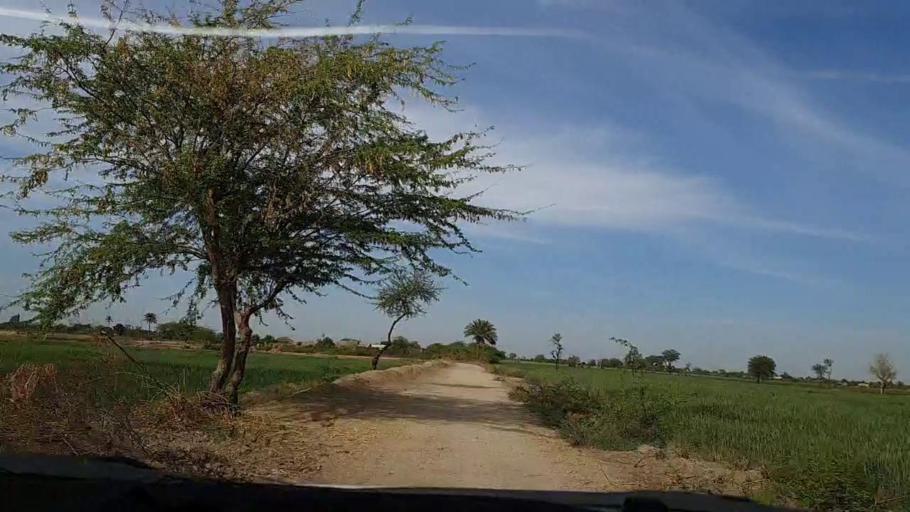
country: PK
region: Sindh
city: Dhoro Naro
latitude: 25.5062
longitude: 69.5194
